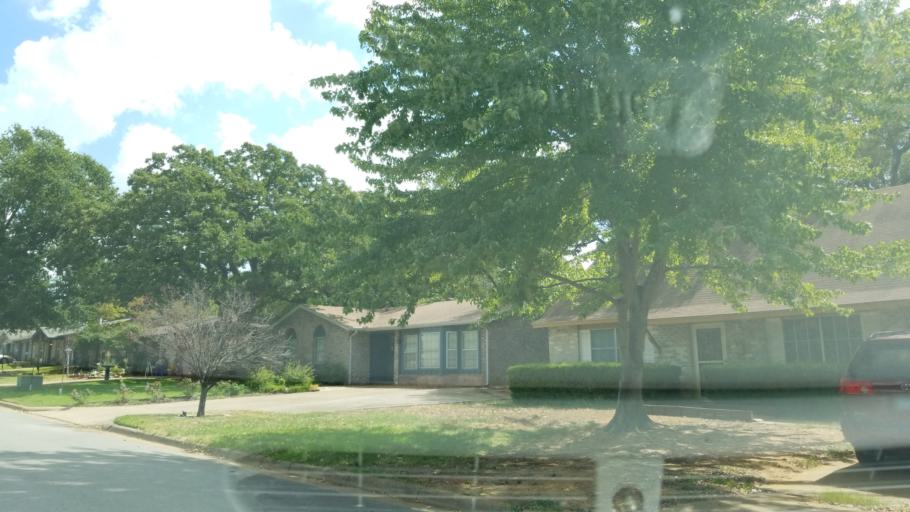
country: US
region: Texas
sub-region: Tarrant County
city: Euless
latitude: 32.8570
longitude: -97.0957
